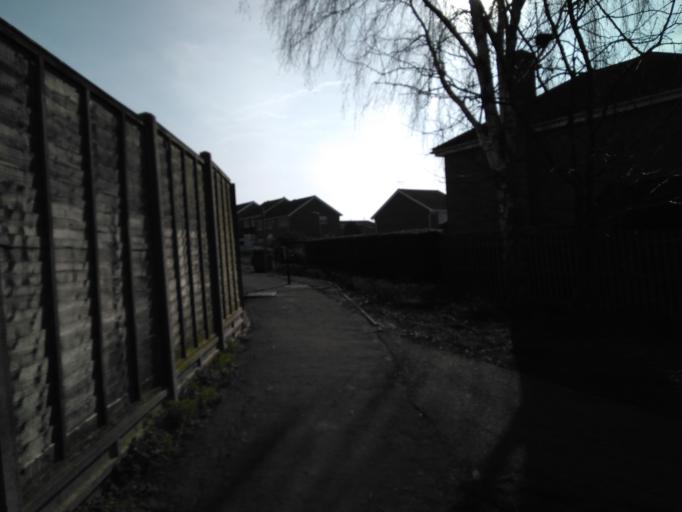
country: GB
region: England
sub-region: Kent
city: Whitstable
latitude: 51.3460
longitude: 1.0125
